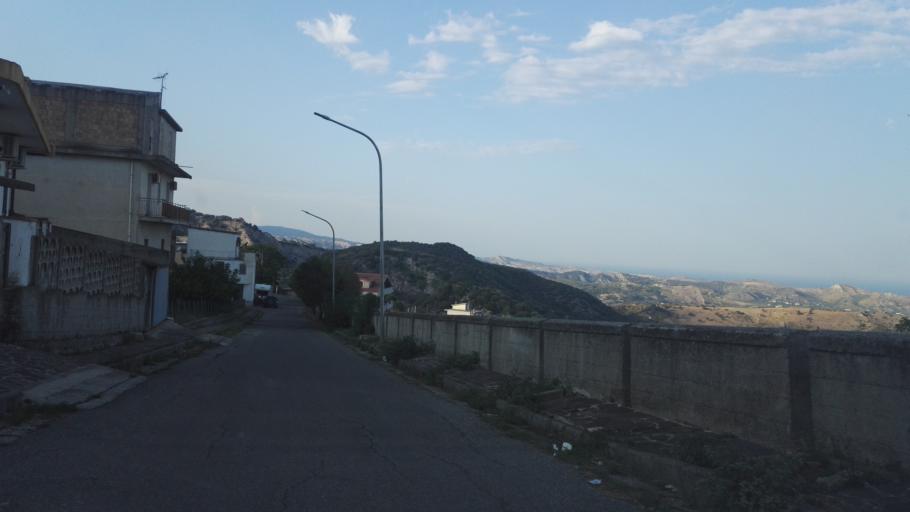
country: IT
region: Calabria
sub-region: Provincia di Reggio Calabria
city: Camini
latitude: 38.4319
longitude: 16.4837
